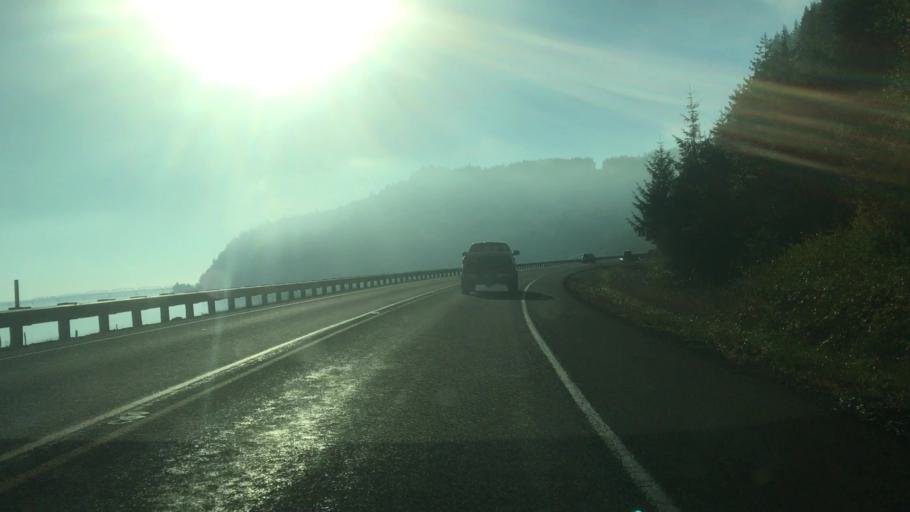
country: US
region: Oregon
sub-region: Clatsop County
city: Astoria
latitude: 46.2622
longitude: -123.8410
